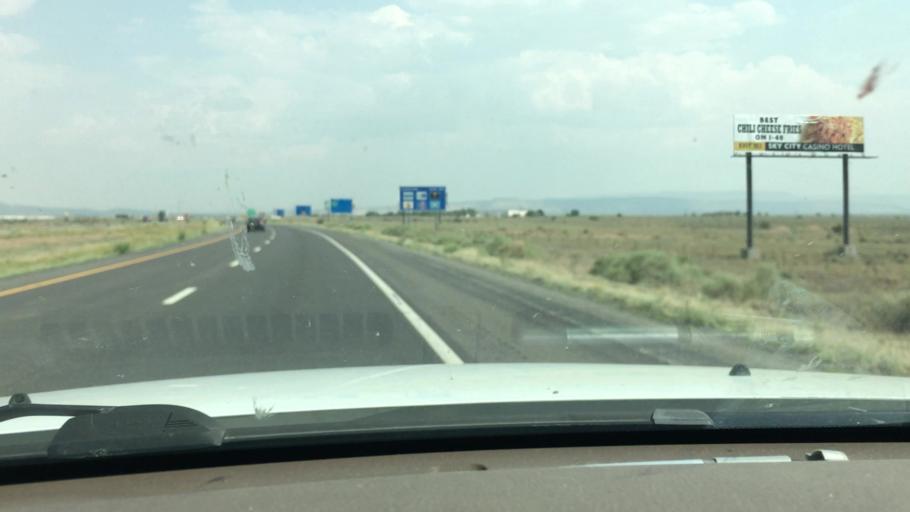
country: US
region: New Mexico
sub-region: Cibola County
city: Grants
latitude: 35.1313
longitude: -107.8406
